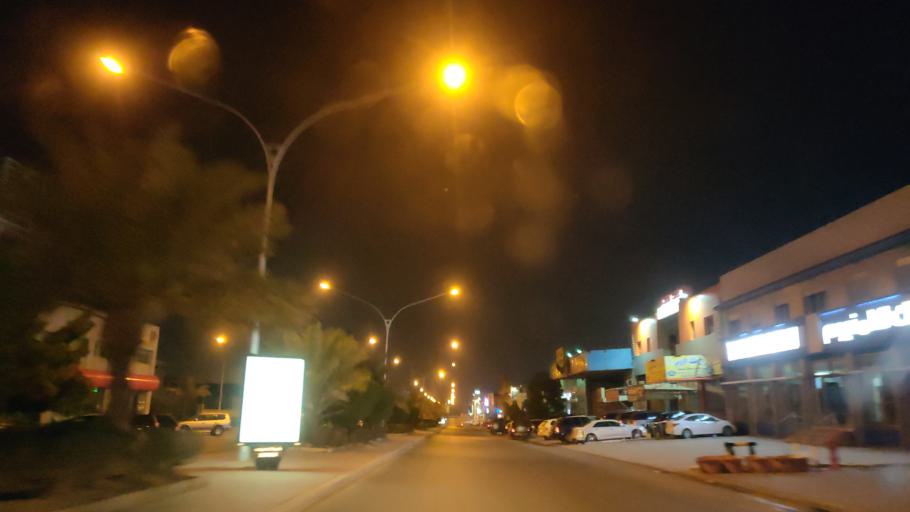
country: KW
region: Al Asimah
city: Ar Rabiyah
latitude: 29.3086
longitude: 47.9354
